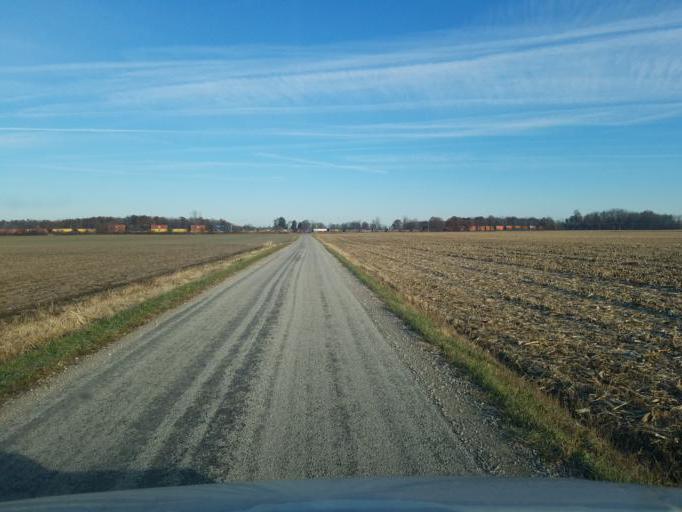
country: US
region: Ohio
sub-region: Morrow County
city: Mount Gilead
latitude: 40.6483
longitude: -82.9387
